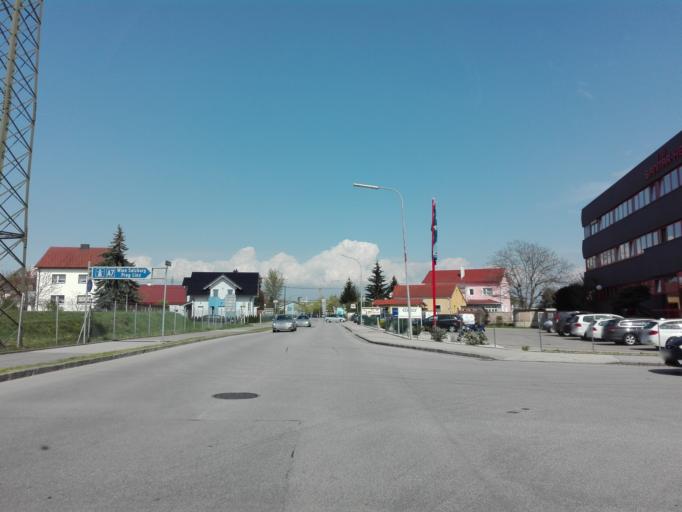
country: AT
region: Upper Austria
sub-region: Politischer Bezirk Linz-Land
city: Ansfelden
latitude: 48.2383
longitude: 14.2740
